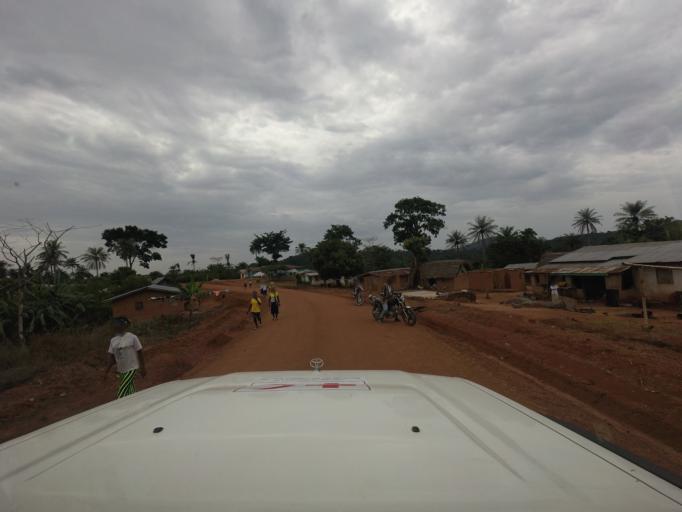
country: SL
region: Eastern Province
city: Buedu
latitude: 8.2142
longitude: -10.2255
